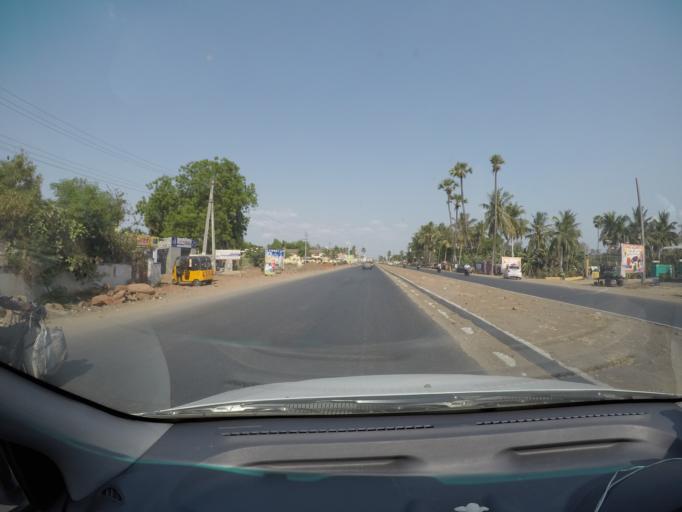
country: IN
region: Andhra Pradesh
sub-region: Krishna
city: Yanamalakuduru
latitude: 16.4747
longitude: 80.7112
